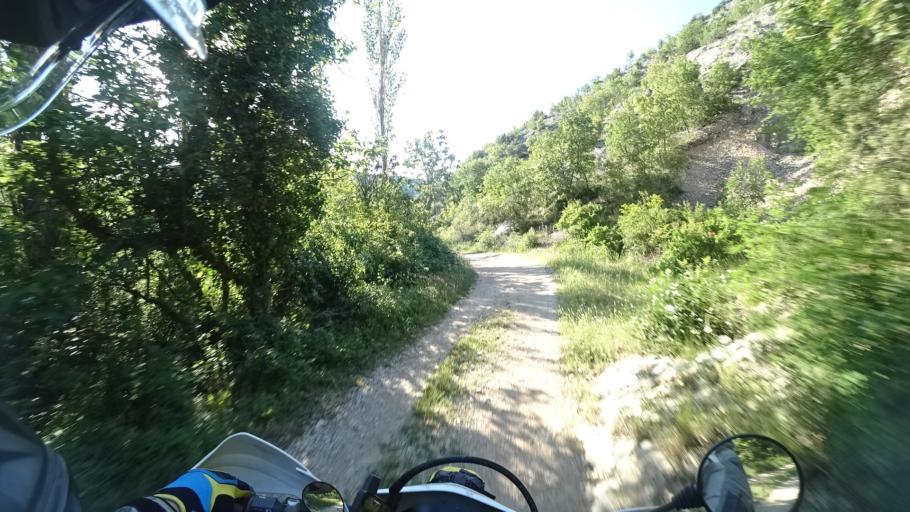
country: HR
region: Sibensko-Kniniska
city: Drnis
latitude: 43.8194
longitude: 16.0200
